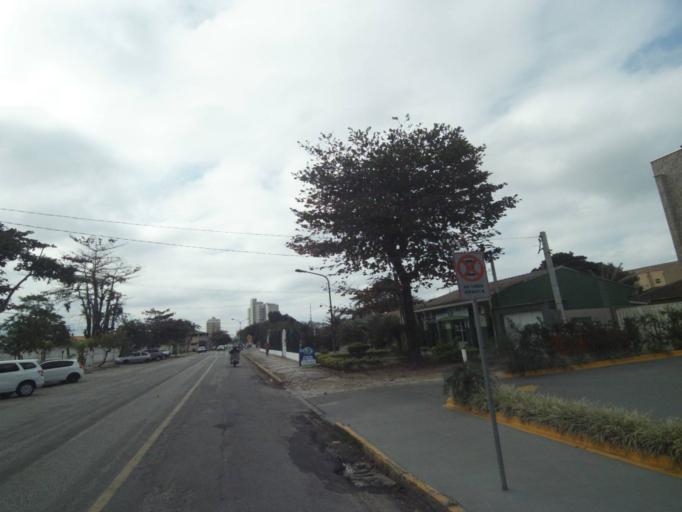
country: BR
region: Parana
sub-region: Paranagua
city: Paranagua
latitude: -25.5222
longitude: -48.5154
